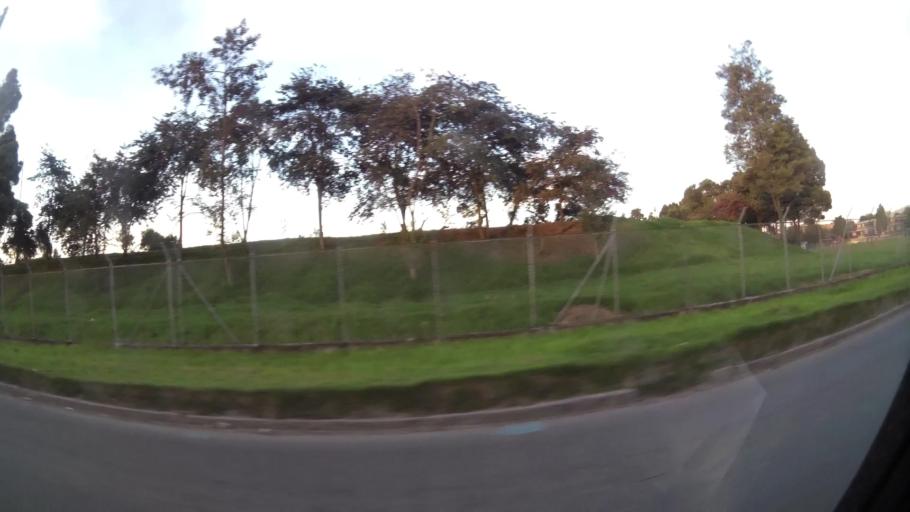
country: CO
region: Cundinamarca
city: Funza
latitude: 4.6837
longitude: -74.1366
